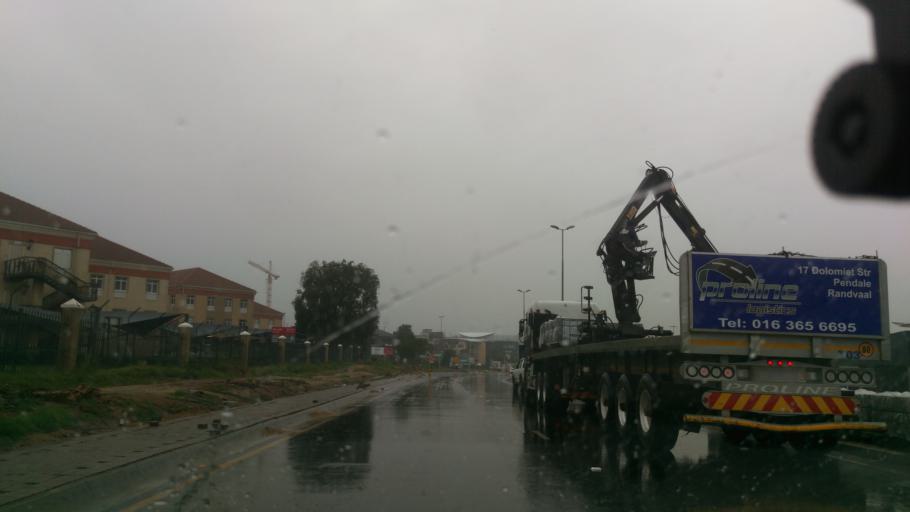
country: ZA
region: Gauteng
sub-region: City of Johannesburg Metropolitan Municipality
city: Diepsloot
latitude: -26.0171
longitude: 28.0011
